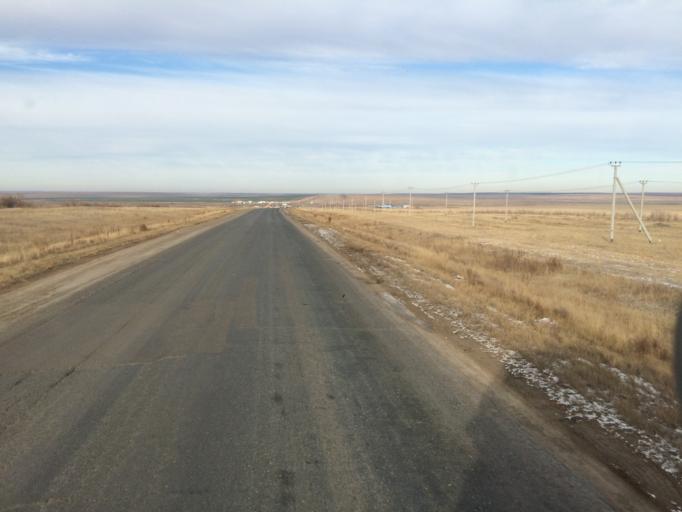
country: KZ
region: Batys Qazaqstan
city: Peremetnoe
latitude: 51.6519
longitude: 51.0109
